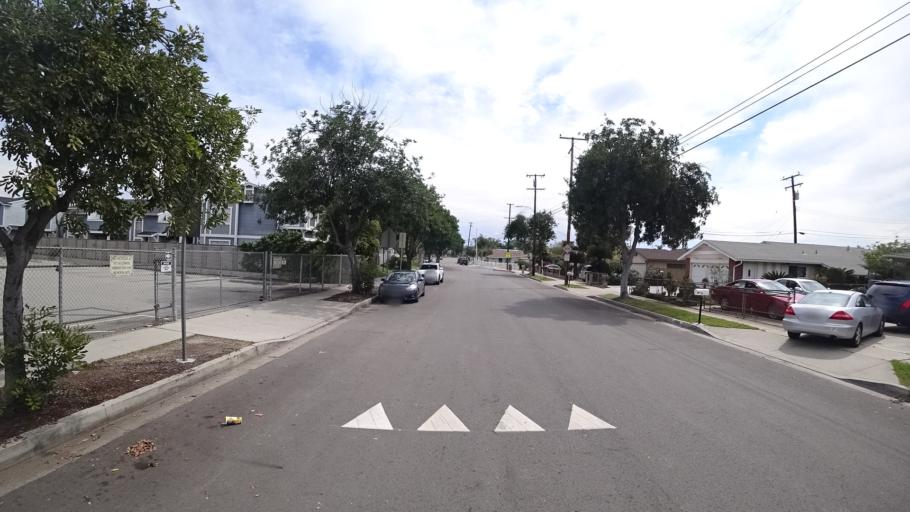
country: US
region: California
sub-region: Los Angeles County
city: West Puente Valley
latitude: 34.0705
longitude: -117.9847
